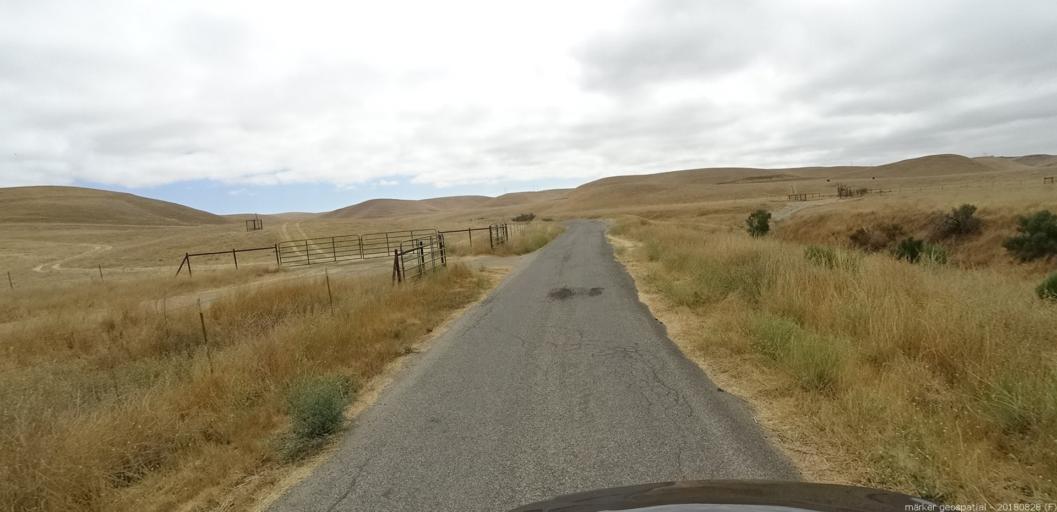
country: US
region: California
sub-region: San Luis Obispo County
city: Lake Nacimiento
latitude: 35.9772
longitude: -120.8664
